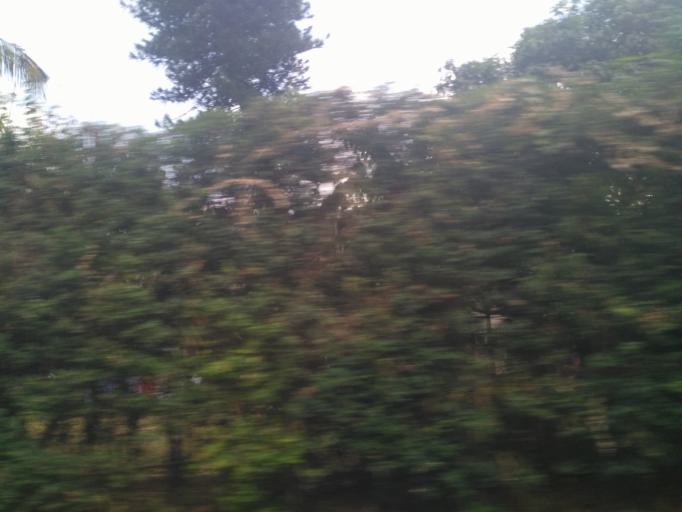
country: TZ
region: Dar es Salaam
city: Dar es Salaam
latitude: -6.7999
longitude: 39.2863
